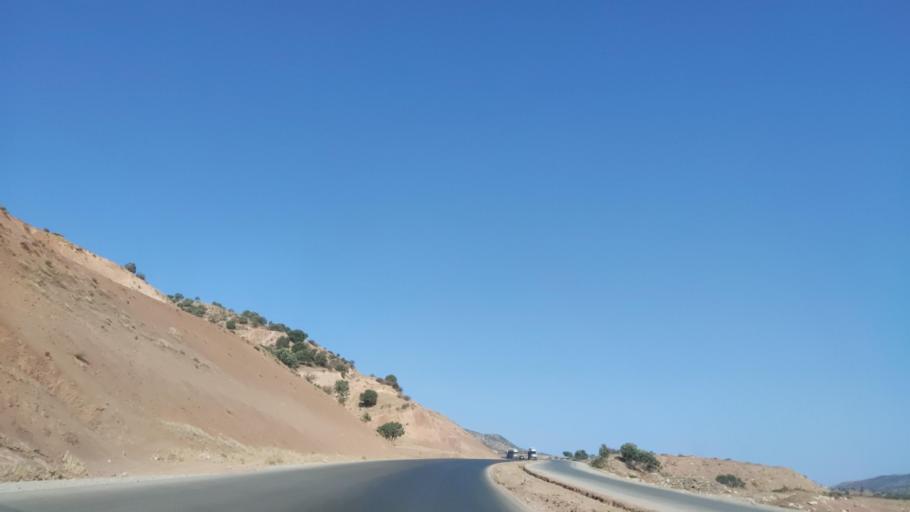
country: IQ
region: Arbil
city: Shaqlawah
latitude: 36.4315
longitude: 44.3139
